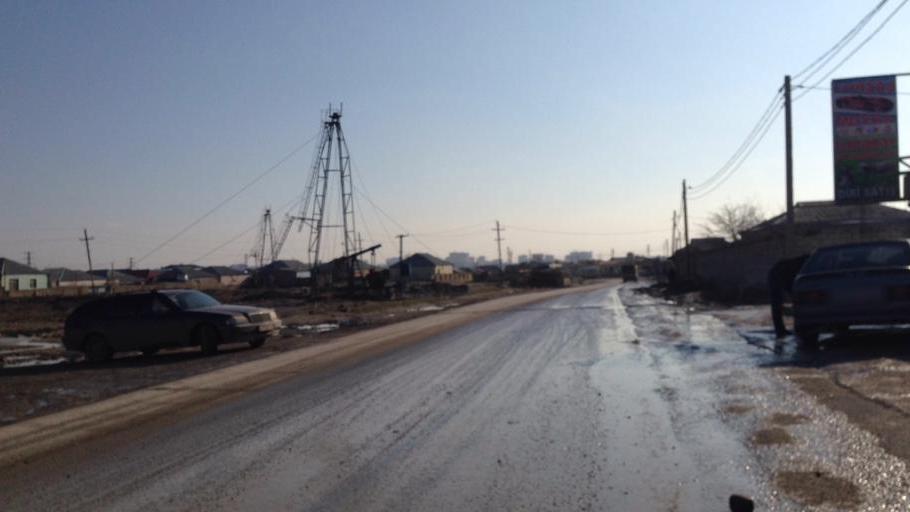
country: AZ
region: Baki
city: Sabuncu
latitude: 40.4502
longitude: 49.9316
